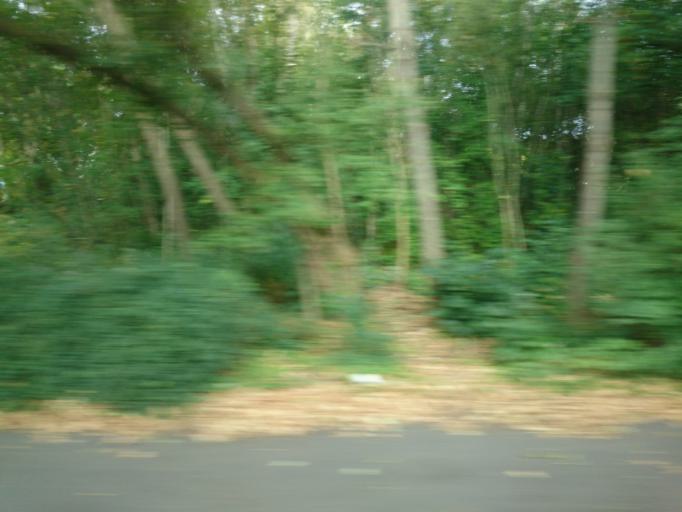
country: DE
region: Berlin
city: Weissensee
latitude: 52.5663
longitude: 13.4721
